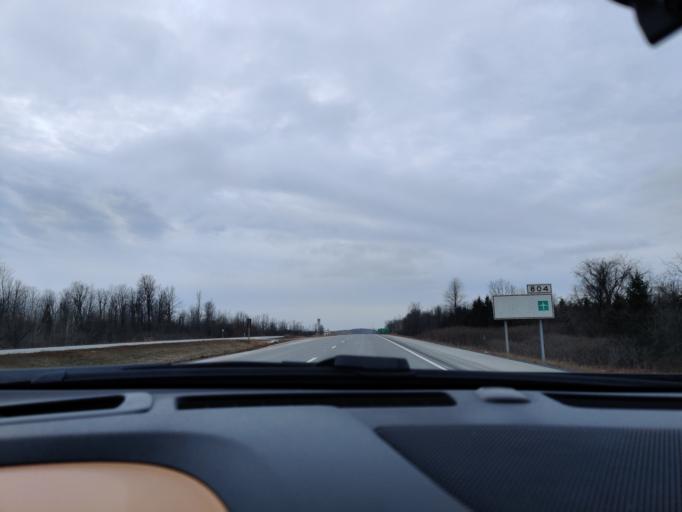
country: CA
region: Ontario
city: Cornwall
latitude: 45.0994
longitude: -74.5752
